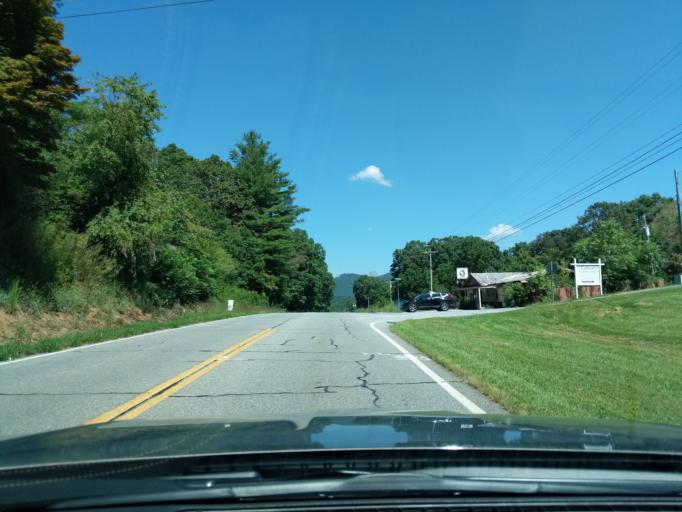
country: US
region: Georgia
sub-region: Towns County
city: Hiawassee
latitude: 34.9093
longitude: -83.7255
